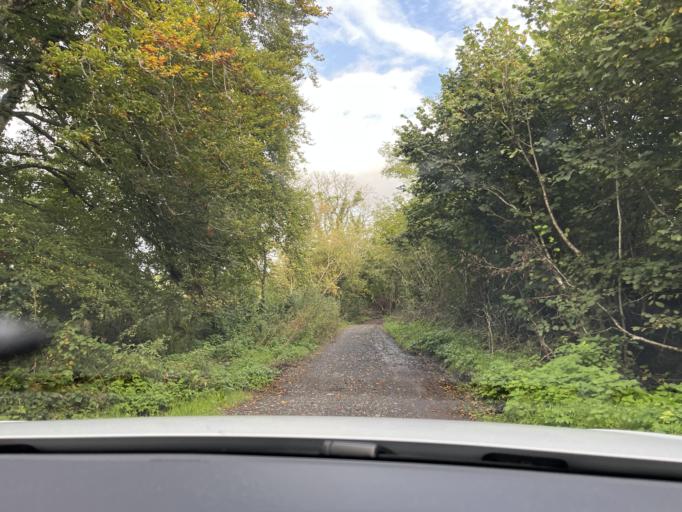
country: IE
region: Connaught
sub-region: County Leitrim
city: Carrick-on-Shannon
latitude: 53.9742
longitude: -8.0727
